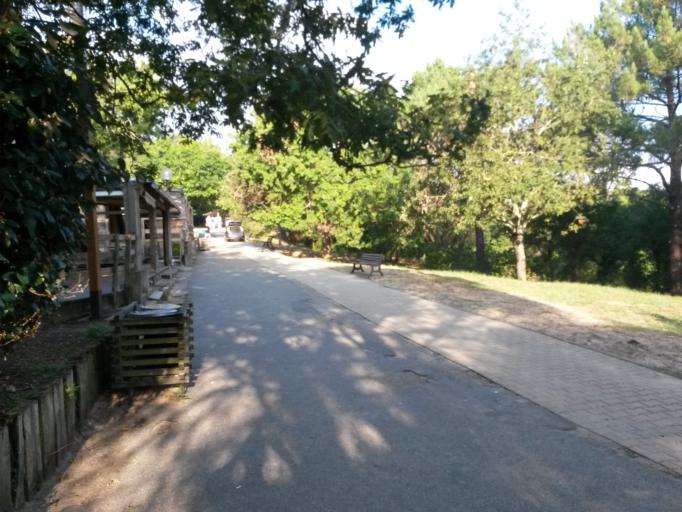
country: FR
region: Aquitaine
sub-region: Departement de la Gironde
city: Arcachon
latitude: 44.5982
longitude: -1.2005
